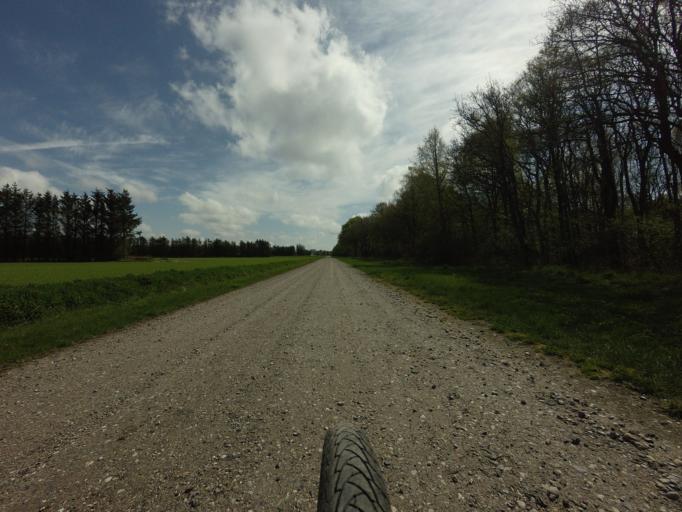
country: DK
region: North Denmark
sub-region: Jammerbugt Kommune
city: Kas
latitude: 57.1998
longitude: 9.6104
